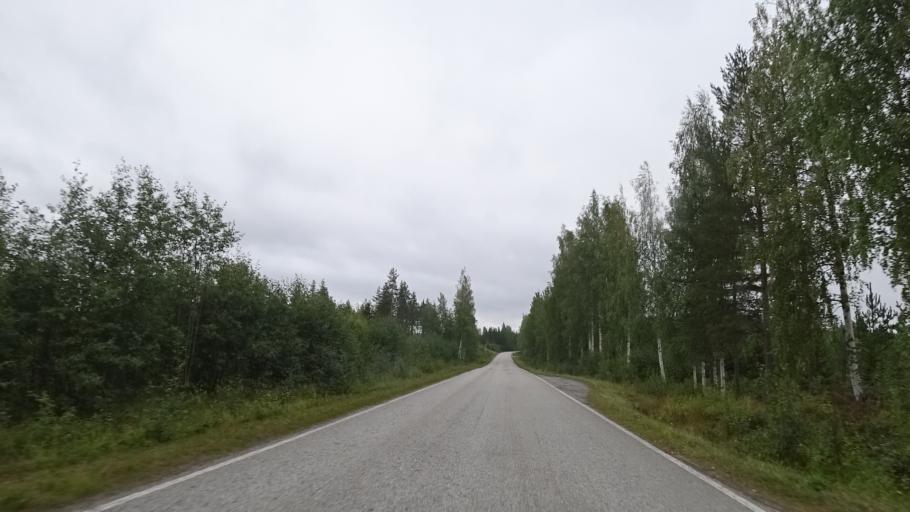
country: FI
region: North Karelia
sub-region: Pielisen Karjala
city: Lieksa
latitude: 63.3541
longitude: 30.2634
